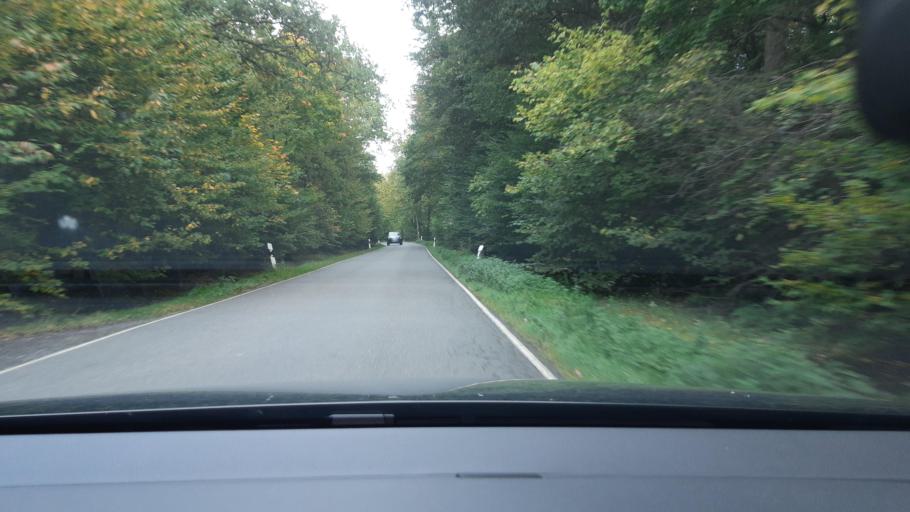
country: DE
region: Hesse
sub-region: Regierungsbezirk Giessen
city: Wetzlar
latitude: 50.5294
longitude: 8.5161
